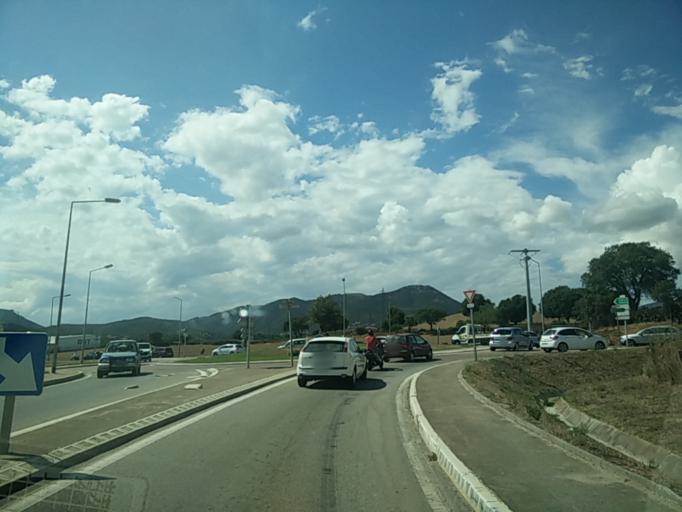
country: FR
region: Corsica
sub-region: Departement de la Corse-du-Sud
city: Afa
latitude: 41.9551
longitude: 8.7965
